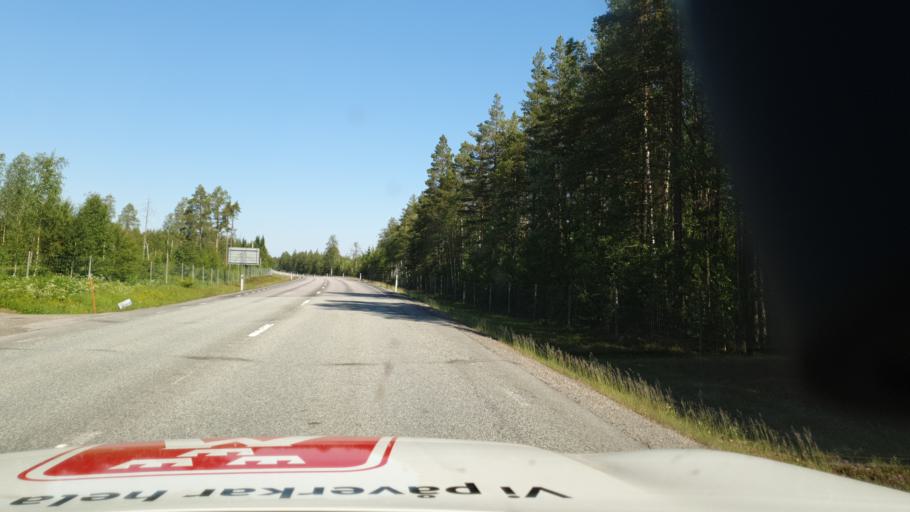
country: SE
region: Vaesterbotten
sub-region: Skelleftea Kommun
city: Burea
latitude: 64.4678
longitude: 21.2931
